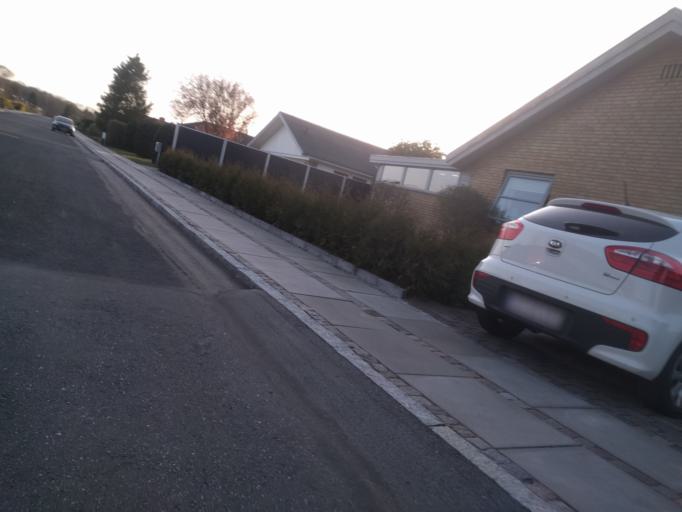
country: DK
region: South Denmark
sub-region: Odense Kommune
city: Bullerup
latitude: 55.4337
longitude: 10.4926
